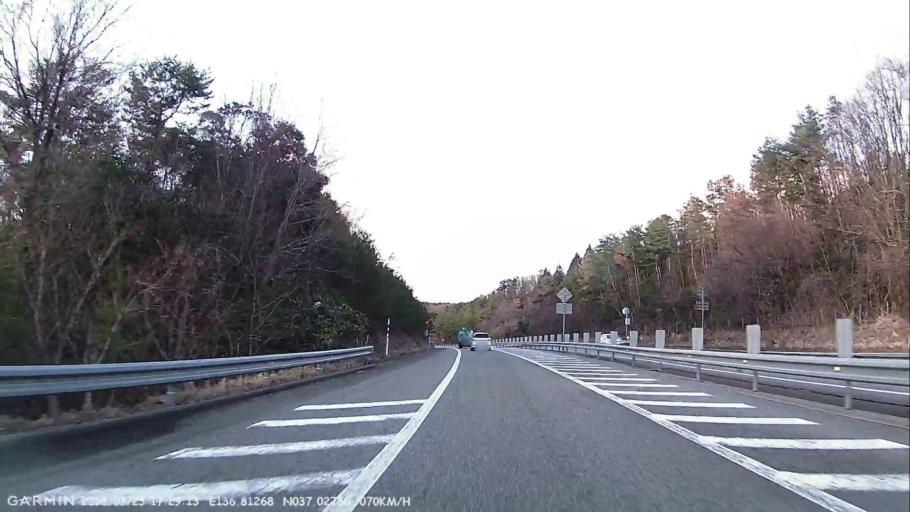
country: JP
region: Ishikawa
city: Hakui
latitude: 37.0278
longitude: 136.8128
